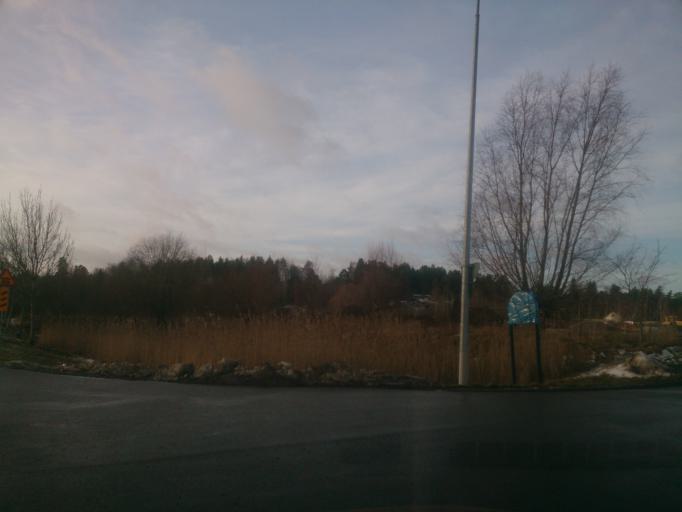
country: SE
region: OEstergoetland
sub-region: Linkopings Kommun
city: Sturefors
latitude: 58.3925
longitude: 15.7040
